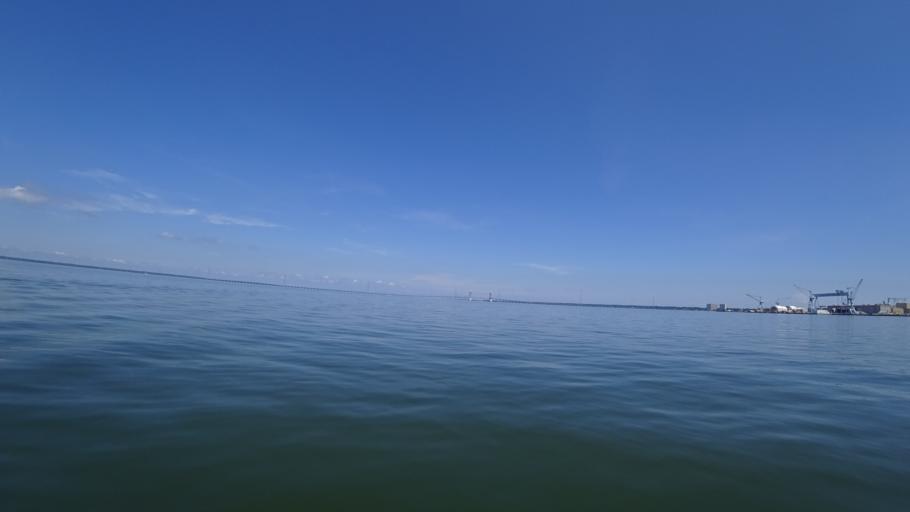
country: US
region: Virginia
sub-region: City of Newport News
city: Newport News
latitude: 36.9853
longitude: -76.4518
